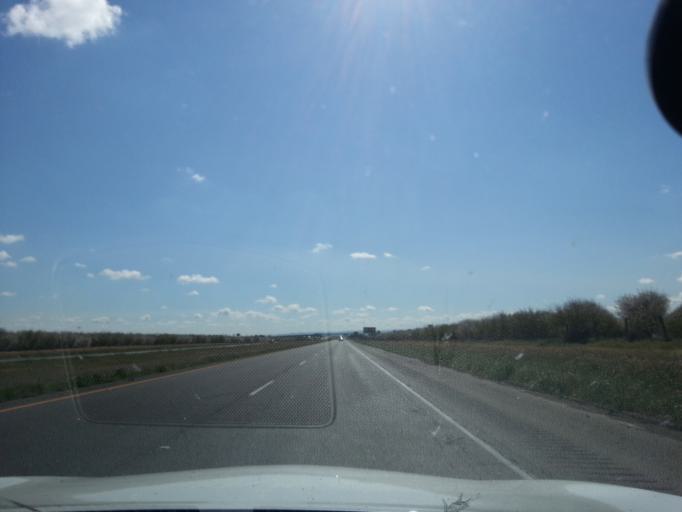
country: US
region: California
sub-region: Fresno County
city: Huron
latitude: 36.2677
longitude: -120.2527
